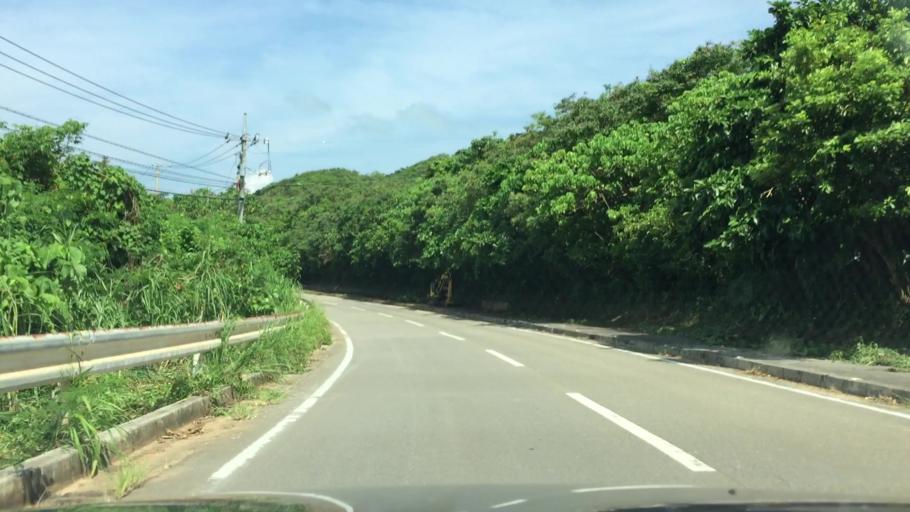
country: JP
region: Okinawa
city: Ishigaki
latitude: 24.4990
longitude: 124.2470
